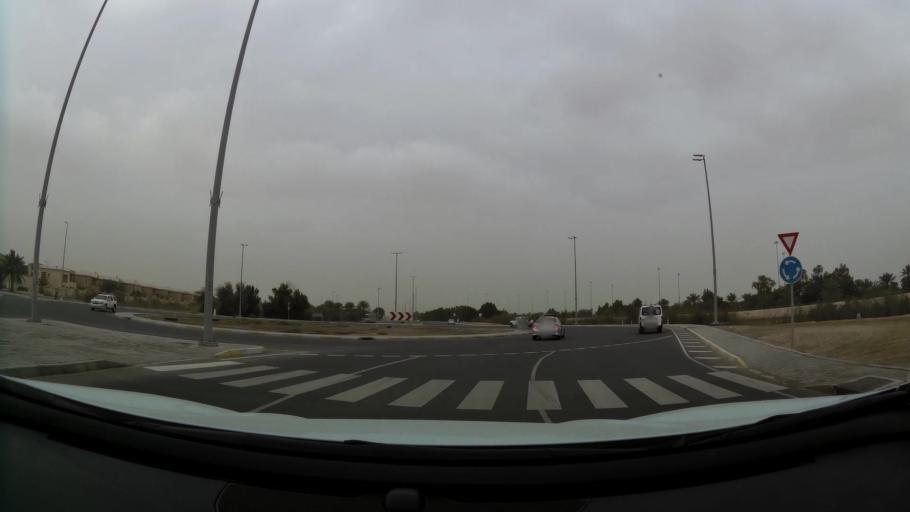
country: AE
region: Abu Dhabi
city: Abu Dhabi
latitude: 24.4239
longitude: 54.5307
